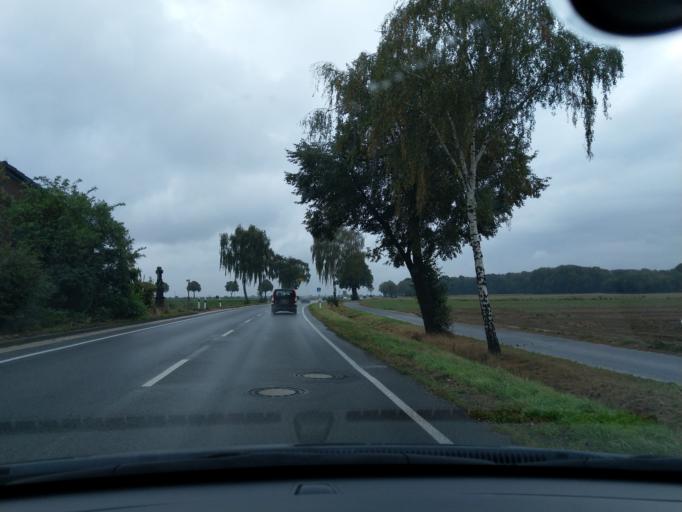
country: DE
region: North Rhine-Westphalia
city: Wegberg
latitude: 51.1213
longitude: 6.2926
